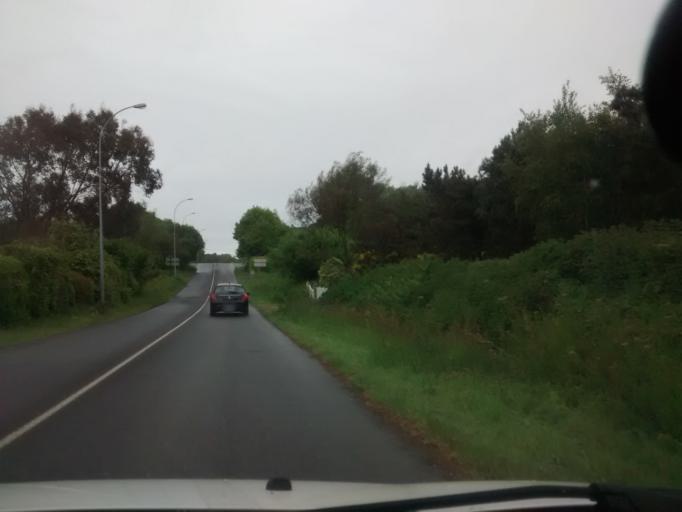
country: FR
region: Brittany
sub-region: Departement des Cotes-d'Armor
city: Penvenan
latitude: 48.8331
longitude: -3.3148
